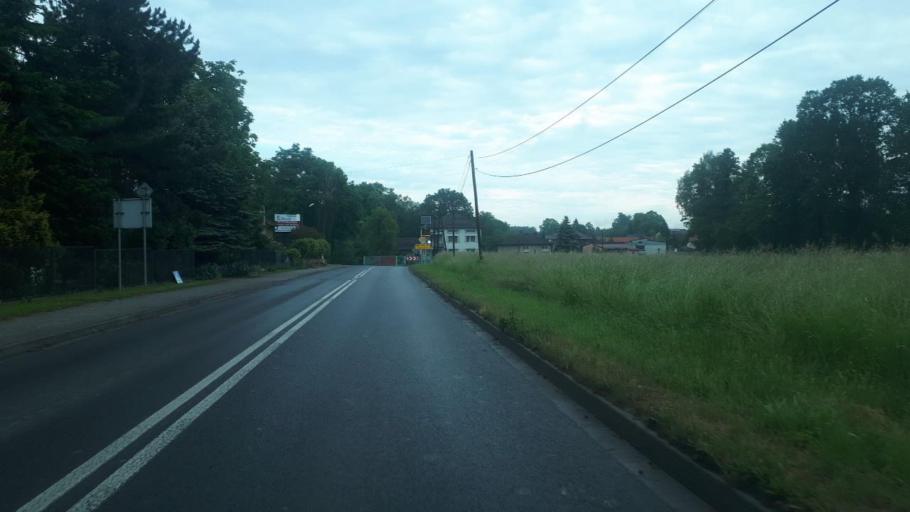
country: PL
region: Lesser Poland Voivodeship
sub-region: Powiat oswiecimski
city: Brzeszcze
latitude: 49.9571
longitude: 19.1373
